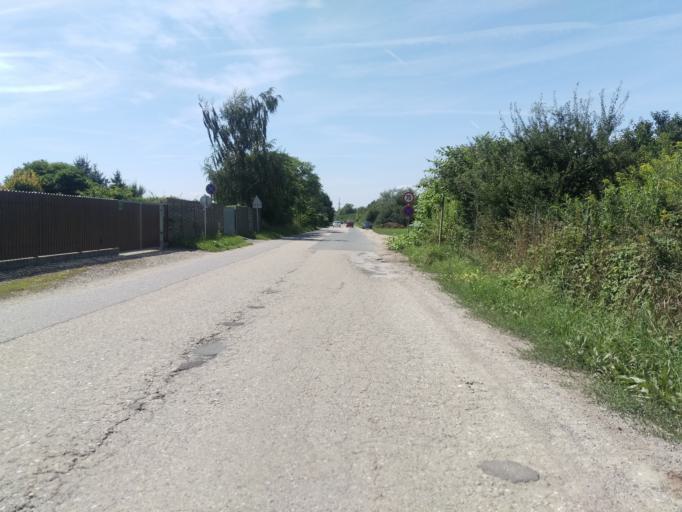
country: AT
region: Styria
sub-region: Politischer Bezirk Graz-Umgebung
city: Seiersberg
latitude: 46.9926
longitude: 15.4215
